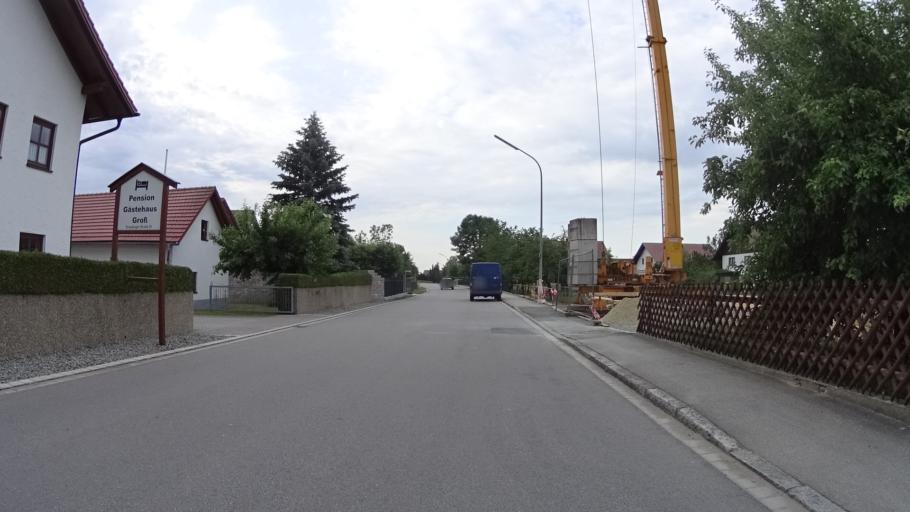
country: DE
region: Bavaria
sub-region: Lower Bavaria
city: Kirchroth
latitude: 48.9278
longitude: 12.5524
